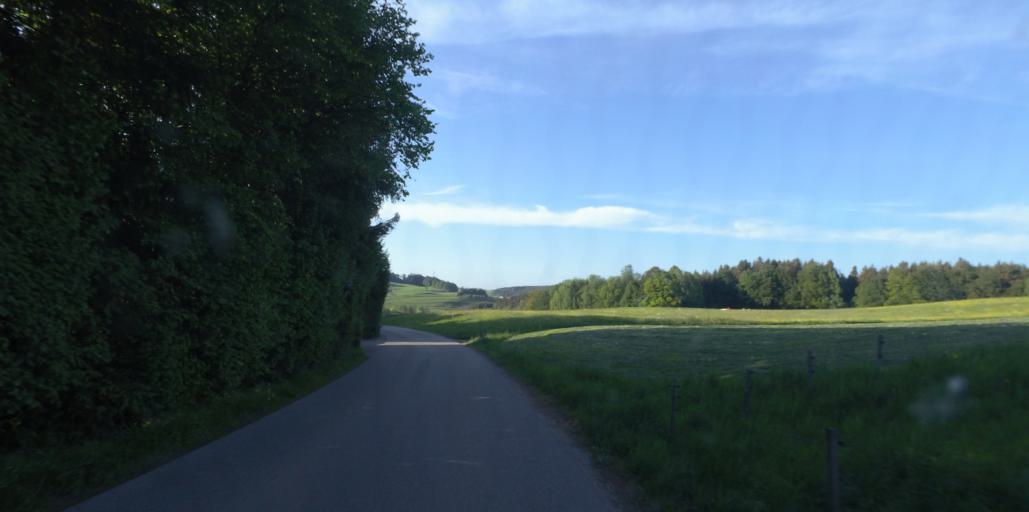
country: DE
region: Bavaria
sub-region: Upper Bavaria
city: Vachendorf
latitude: 47.8416
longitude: 12.5872
